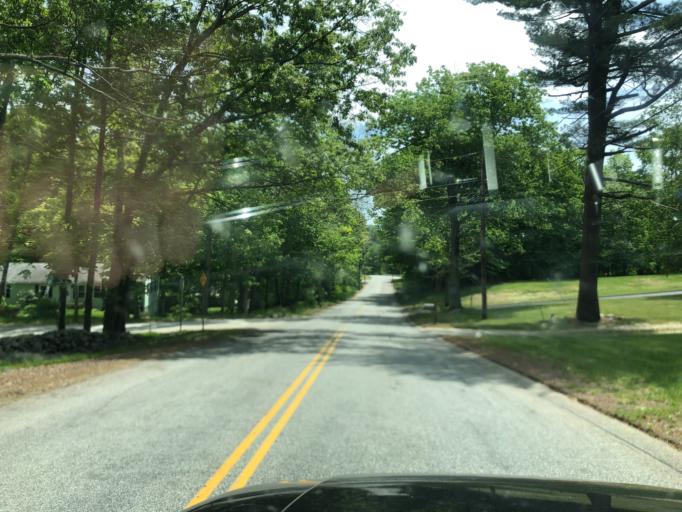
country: US
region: Connecticut
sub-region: Windham County
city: North Grosvenor Dale
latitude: 41.9769
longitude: -71.8880
